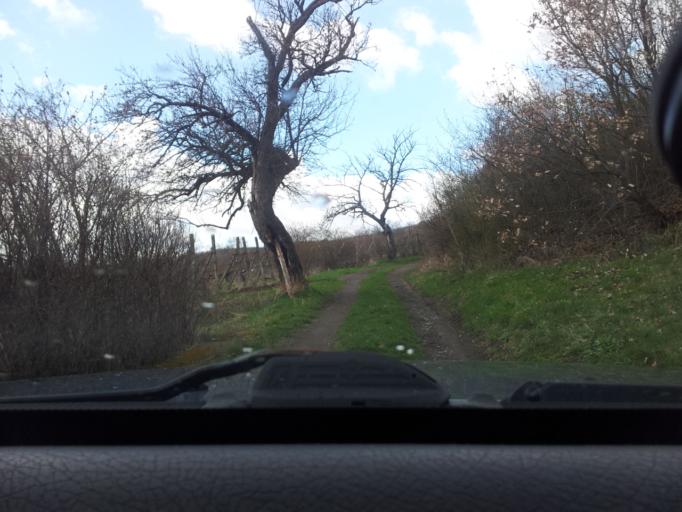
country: SK
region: Nitriansky
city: Tlmace
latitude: 48.3012
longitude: 18.5657
